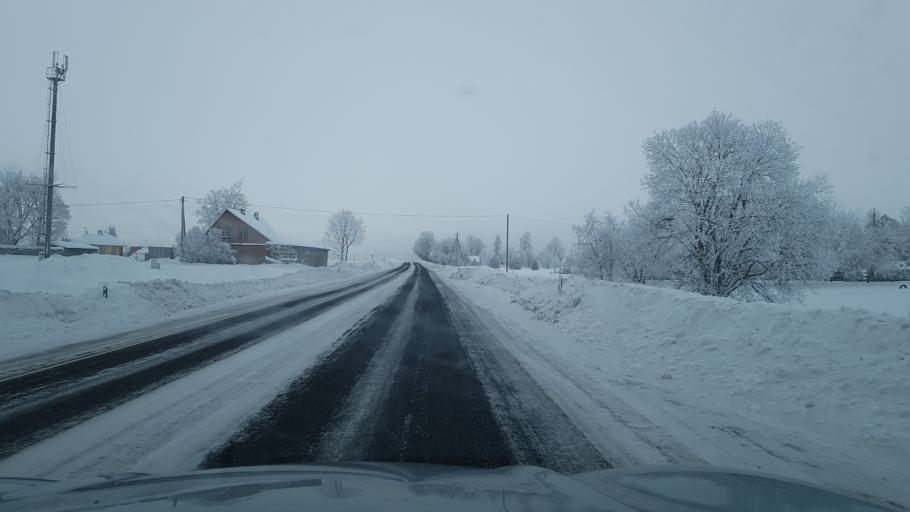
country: EE
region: Ida-Virumaa
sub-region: Johvi vald
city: Johvi
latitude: 59.2595
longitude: 27.3839
